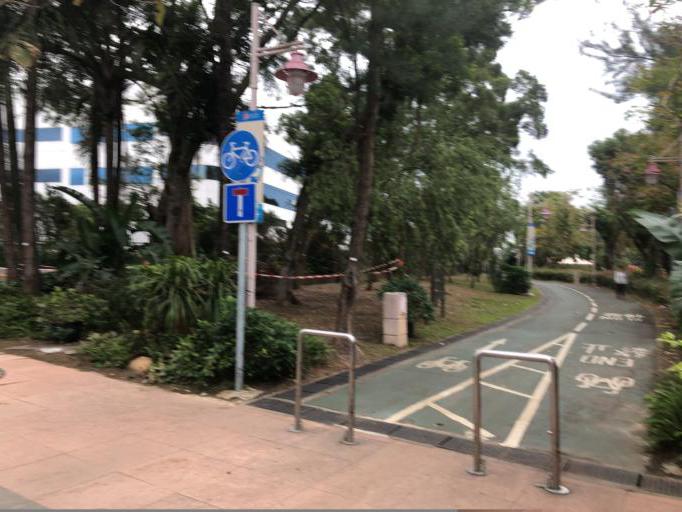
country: HK
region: Tai Po
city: Tai Po
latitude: 22.4516
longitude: 114.1915
